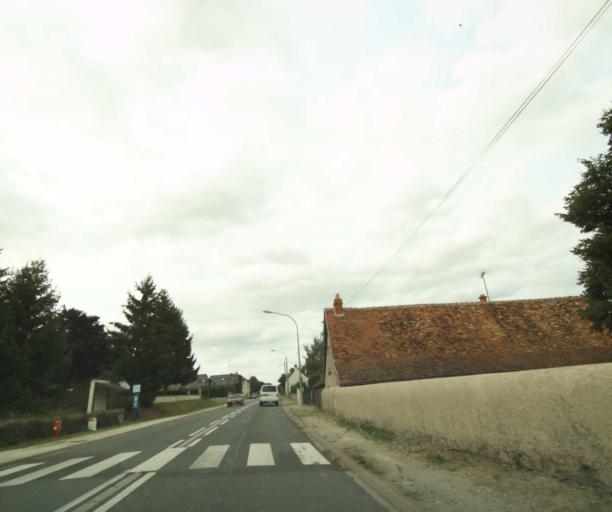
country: FR
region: Centre
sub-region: Departement d'Indre-et-Loire
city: Perrusson
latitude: 47.0598
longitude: 1.0836
